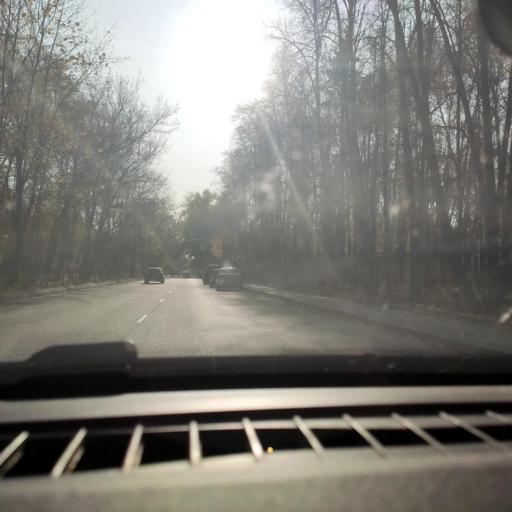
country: RU
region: Voronezj
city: Voronezh
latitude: 51.7176
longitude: 39.2211
